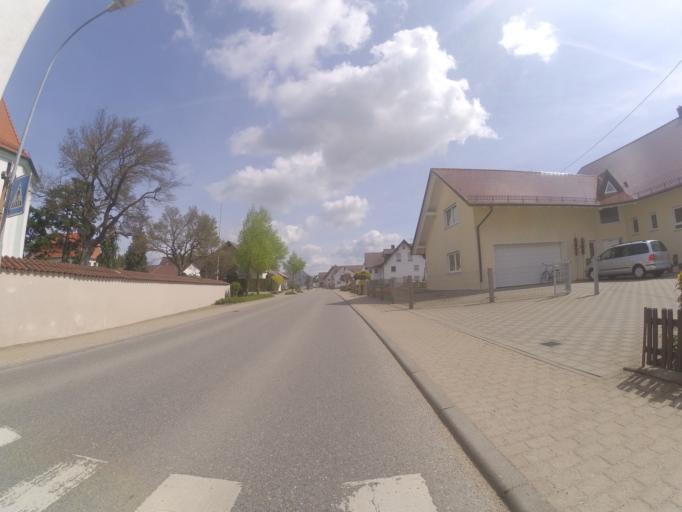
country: DE
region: Baden-Wuerttemberg
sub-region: Tuebingen Region
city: Dettingen
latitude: 48.2321
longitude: 9.7337
